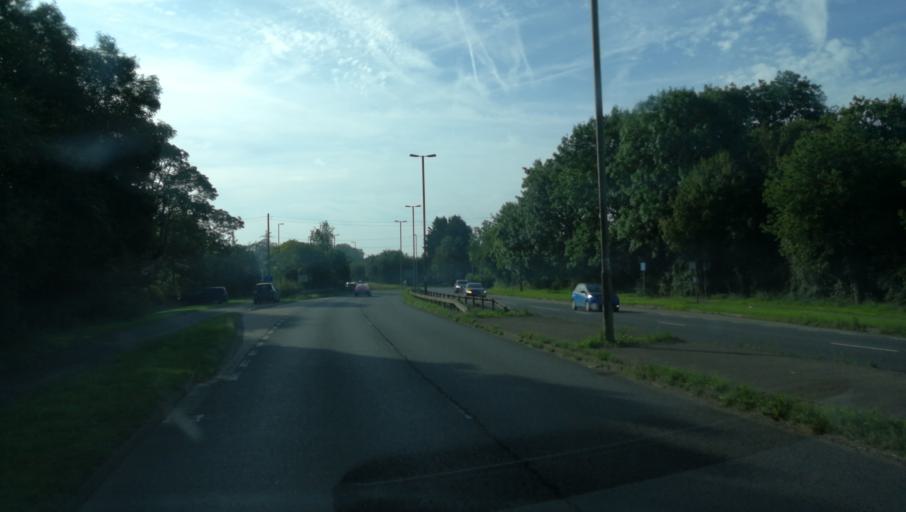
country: GB
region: England
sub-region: Oxfordshire
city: Yarnton
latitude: 51.8079
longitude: -1.3024
